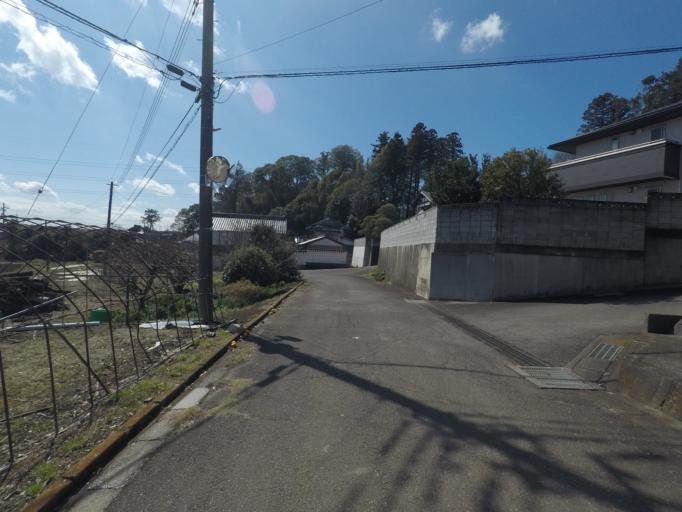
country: JP
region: Ibaraki
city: Ushiku
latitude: 36.0077
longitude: 140.0739
